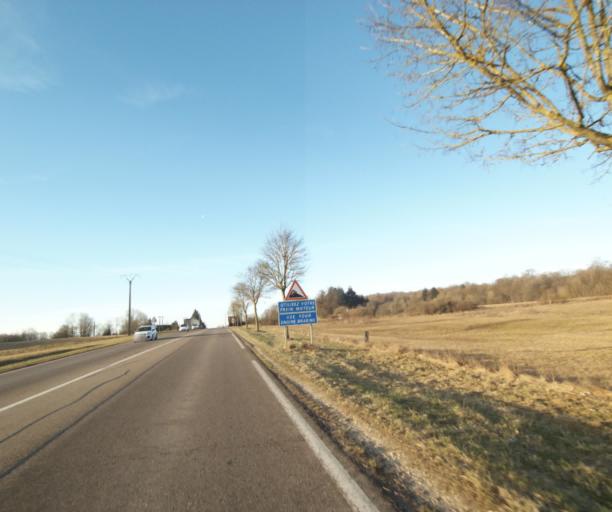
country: FR
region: Lorraine
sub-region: Departement de Meurthe-et-Moselle
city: Chavigny
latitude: 48.6391
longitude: 6.1314
